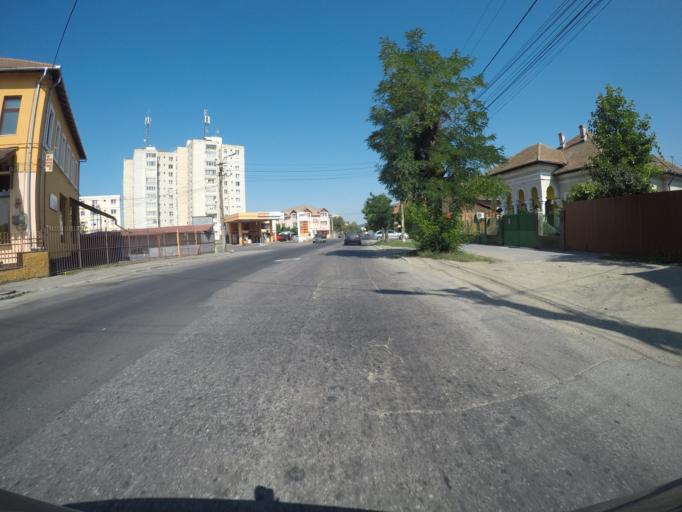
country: RO
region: Brasov
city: Fogarasch
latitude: 45.8310
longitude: 24.9768
